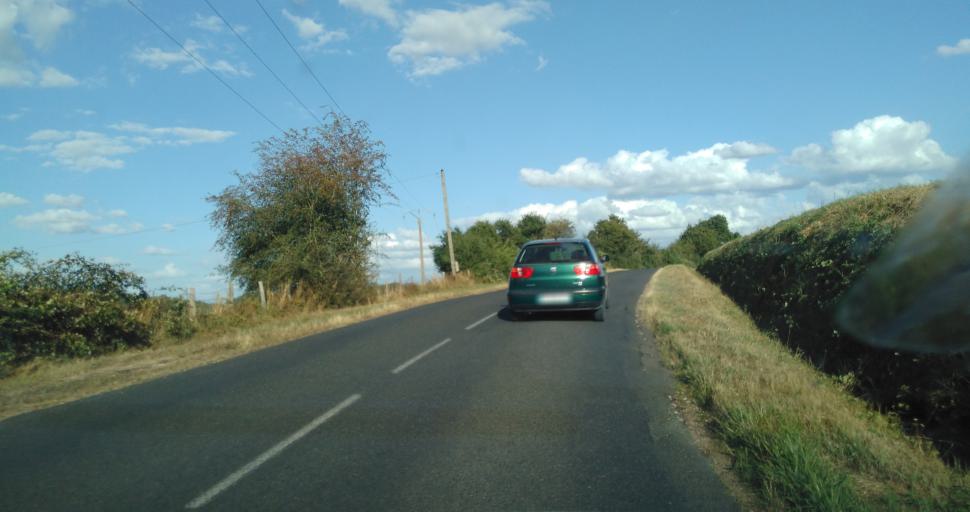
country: FR
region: Centre
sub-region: Departement d'Indre-et-Loire
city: Charge
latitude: 47.4080
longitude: 1.0374
